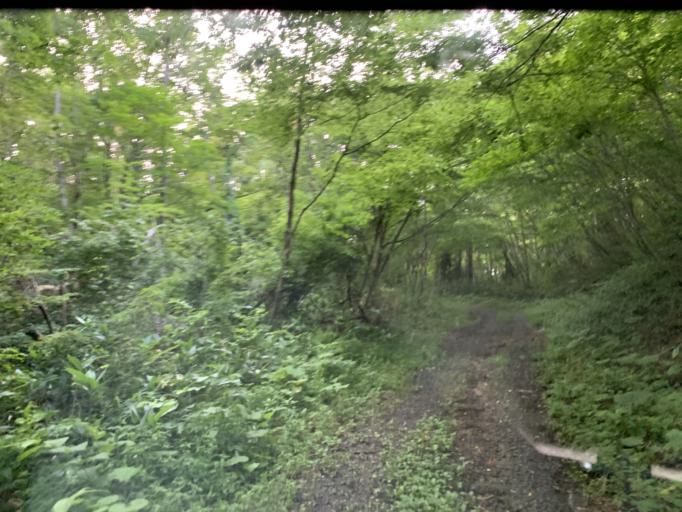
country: JP
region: Iwate
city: Ichinoseki
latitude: 38.9099
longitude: 140.9478
